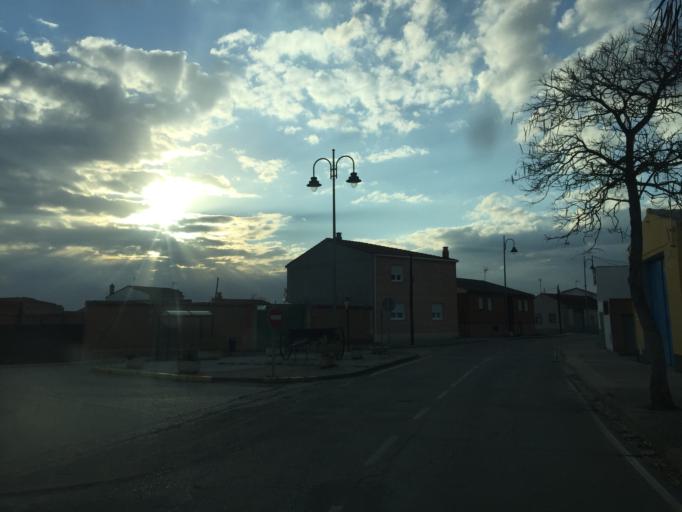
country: ES
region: Castille and Leon
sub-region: Provincia de Palencia
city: Venta de Banos
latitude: 41.9197
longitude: -4.4768
